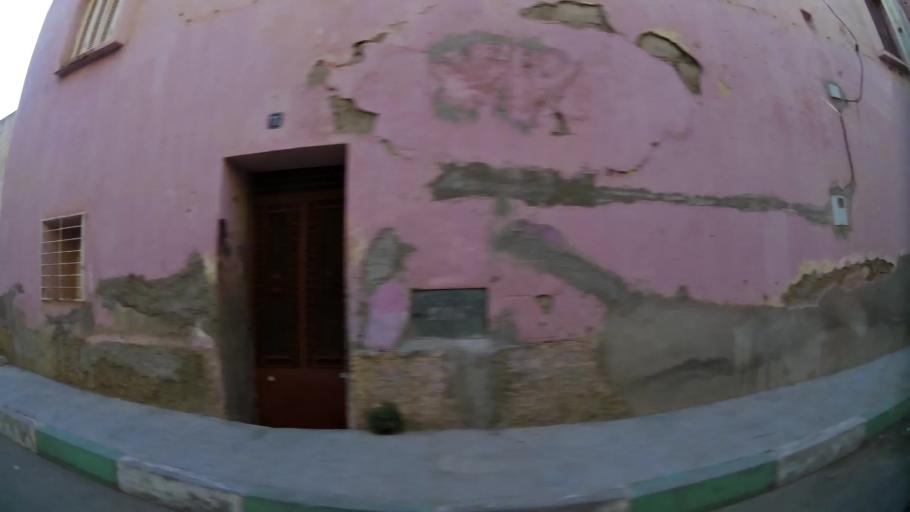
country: MA
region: Oriental
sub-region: Berkane-Taourirt
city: Berkane
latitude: 34.9263
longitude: -2.3197
